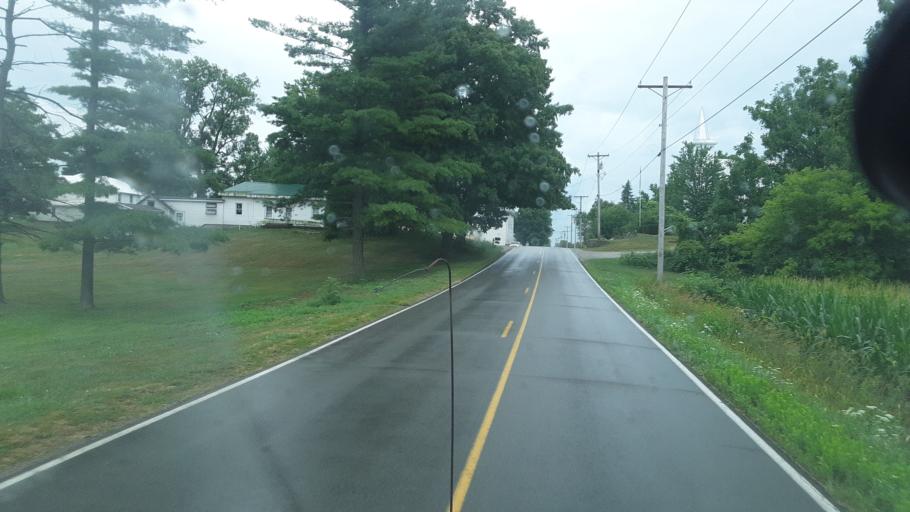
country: US
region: Indiana
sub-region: Steuben County
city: Hamilton
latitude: 41.6176
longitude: -84.8381
